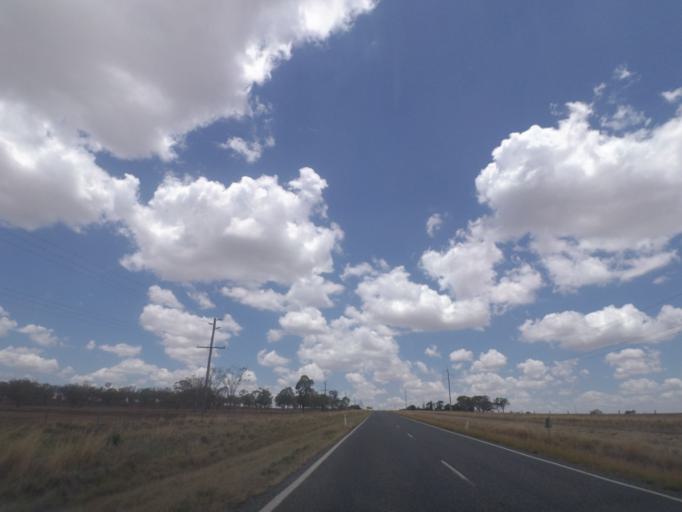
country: AU
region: Queensland
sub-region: Toowoomba
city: Top Camp
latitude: -27.8804
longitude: 151.9696
